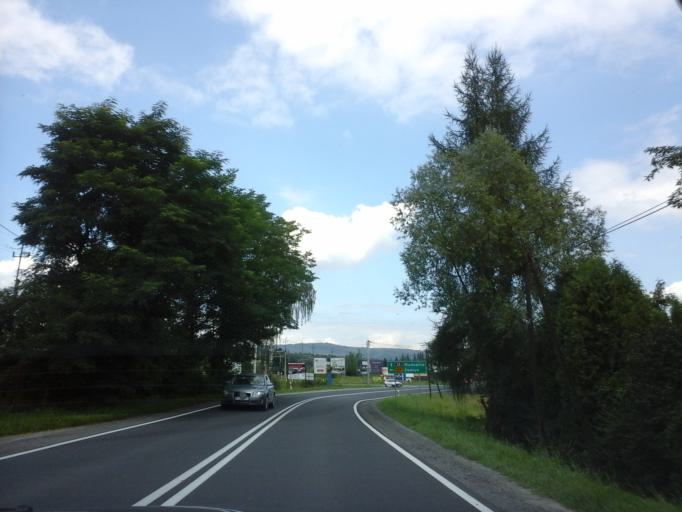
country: PL
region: Lesser Poland Voivodeship
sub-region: Powiat suski
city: Juszczyn
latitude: 49.7093
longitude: 19.6895
